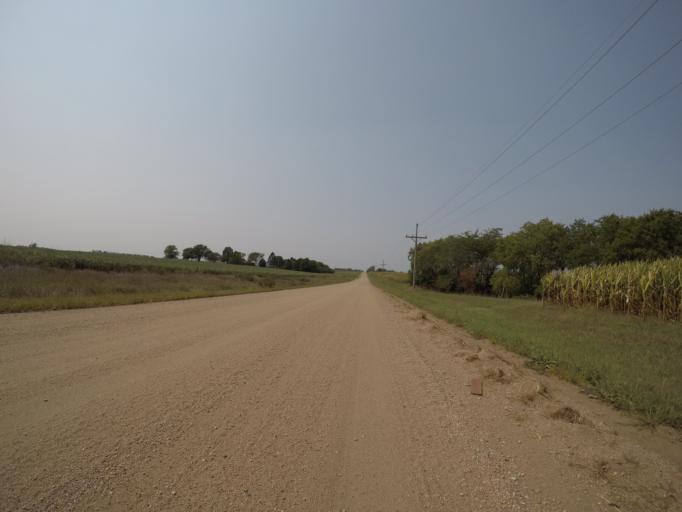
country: US
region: Nebraska
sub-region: Gage County
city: Beatrice
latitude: 40.2774
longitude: -96.7918
